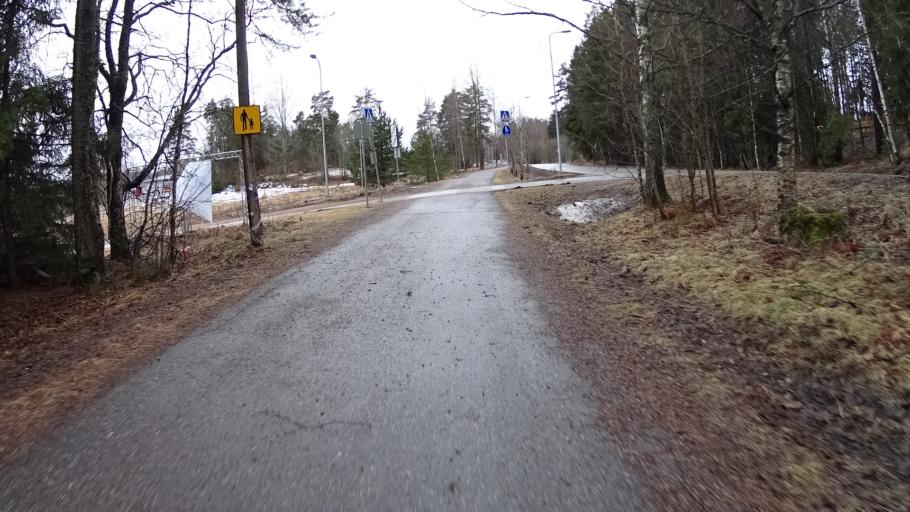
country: FI
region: Uusimaa
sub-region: Helsinki
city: Kauniainen
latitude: 60.2307
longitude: 24.6963
